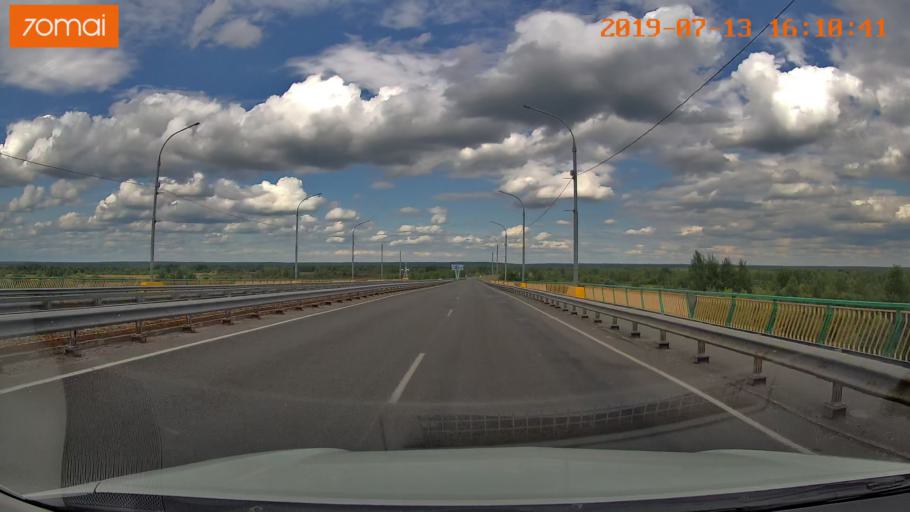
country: BY
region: Mogilev
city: Babruysk
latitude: 53.1622
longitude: 29.2434
